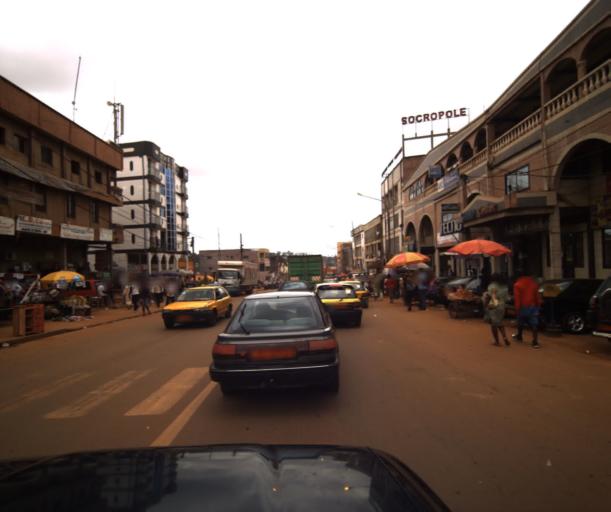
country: CM
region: Centre
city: Yaounde
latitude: 3.8506
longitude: 11.5216
